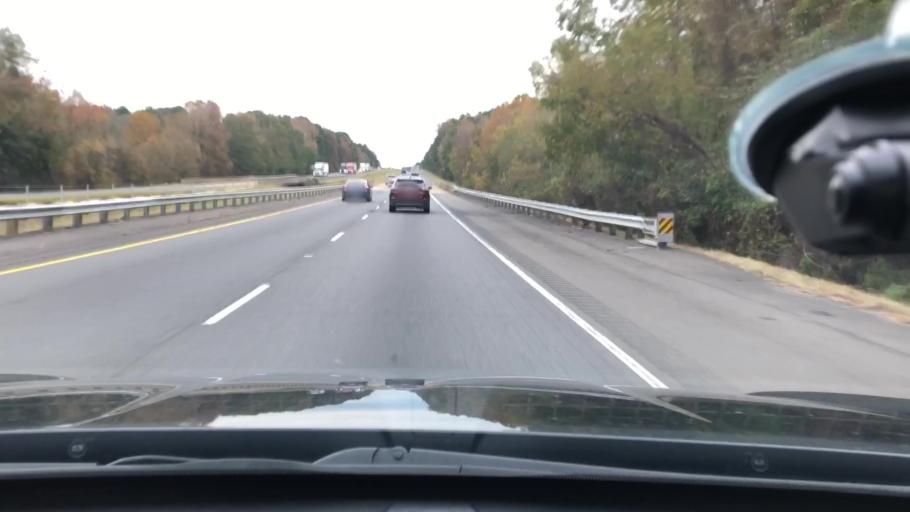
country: US
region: Arkansas
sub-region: Clark County
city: Gurdon
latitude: 34.0270
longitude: -93.1525
